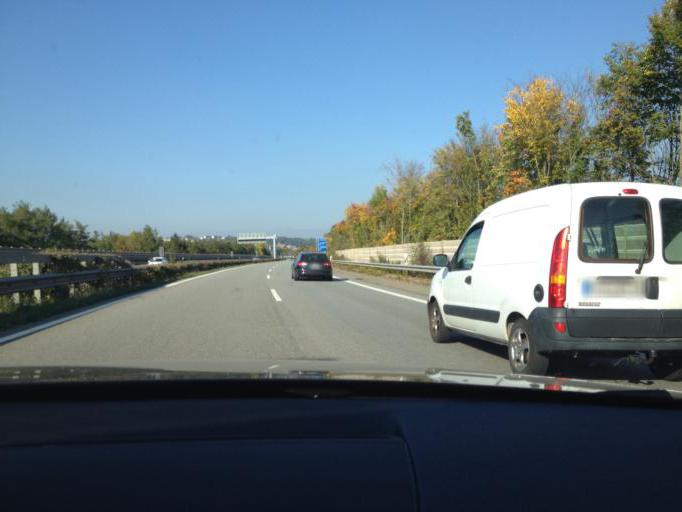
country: DE
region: Rheinland-Pfalz
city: Zweibrucken
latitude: 49.2322
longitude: 7.3589
